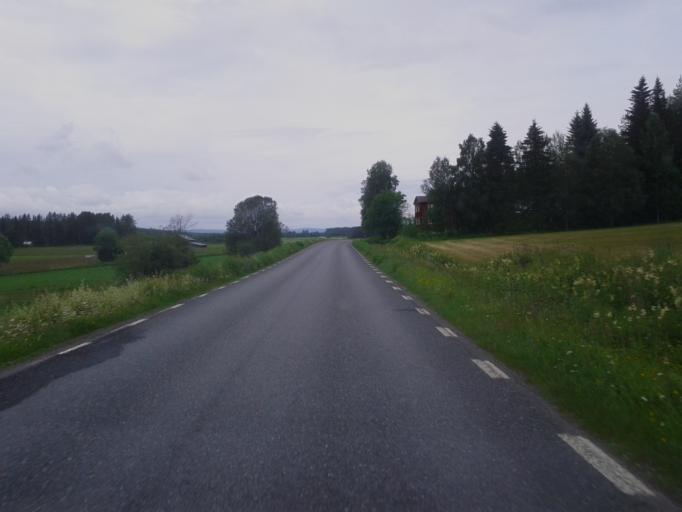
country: SE
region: Vaesterbotten
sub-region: Skelleftea Kommun
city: Viken
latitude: 64.8884
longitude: 20.7468
